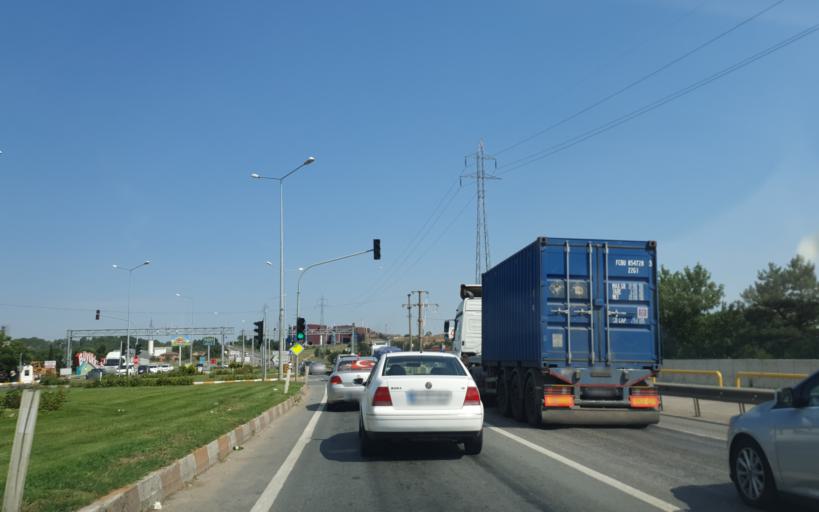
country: TR
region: Kirklareli
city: Buyukkaristiran
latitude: 41.2937
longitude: 27.5409
